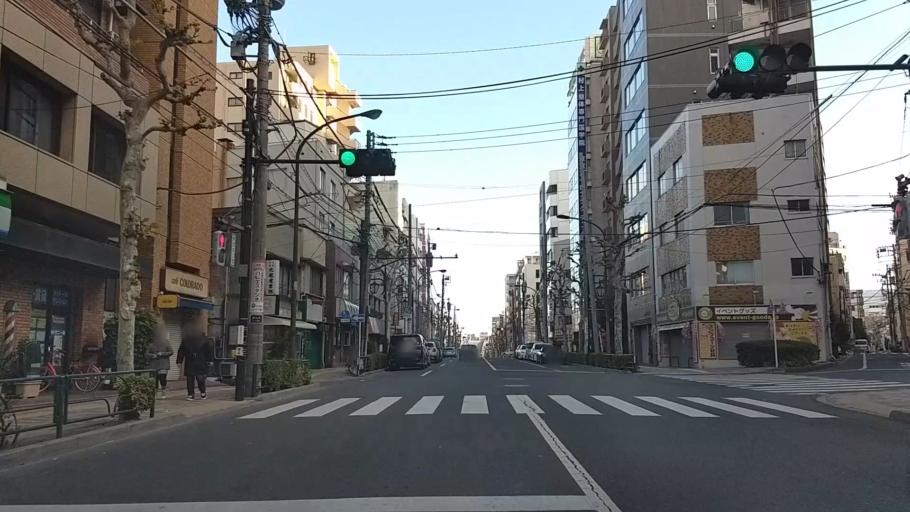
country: JP
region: Tokyo
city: Tokyo
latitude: 35.7295
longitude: 139.7310
